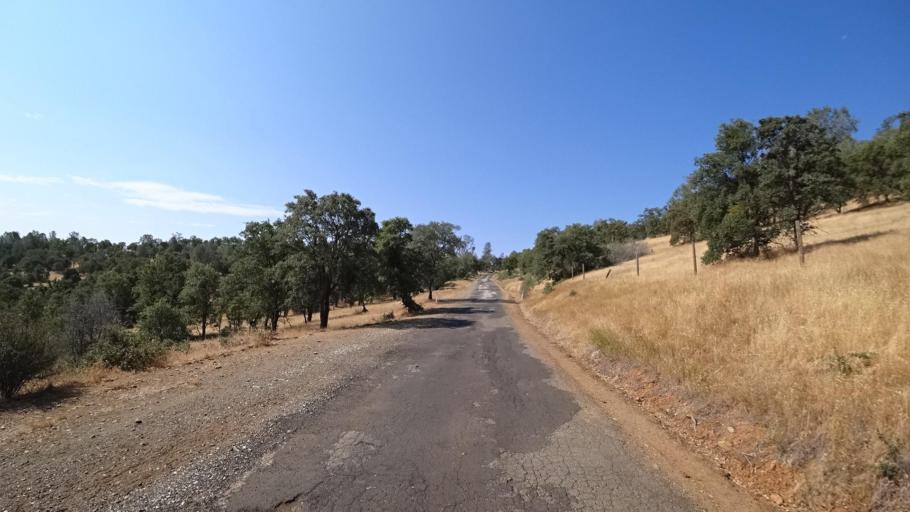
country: US
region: California
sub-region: Tuolumne County
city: Tuolumne City
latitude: 37.7289
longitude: -120.2457
